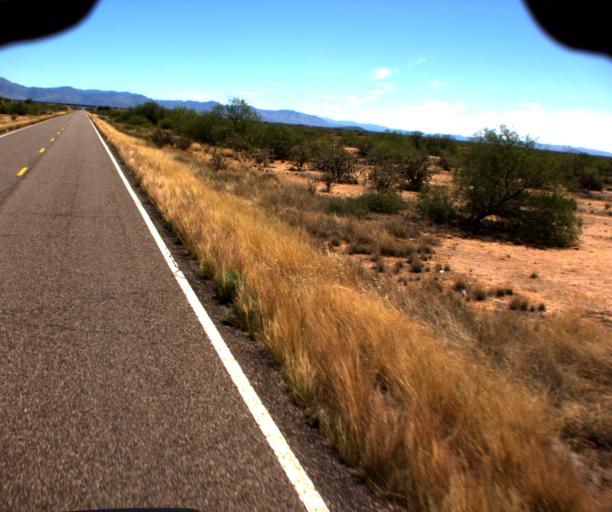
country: US
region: Arizona
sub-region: Yavapai County
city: Congress
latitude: 34.1205
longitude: -112.9579
